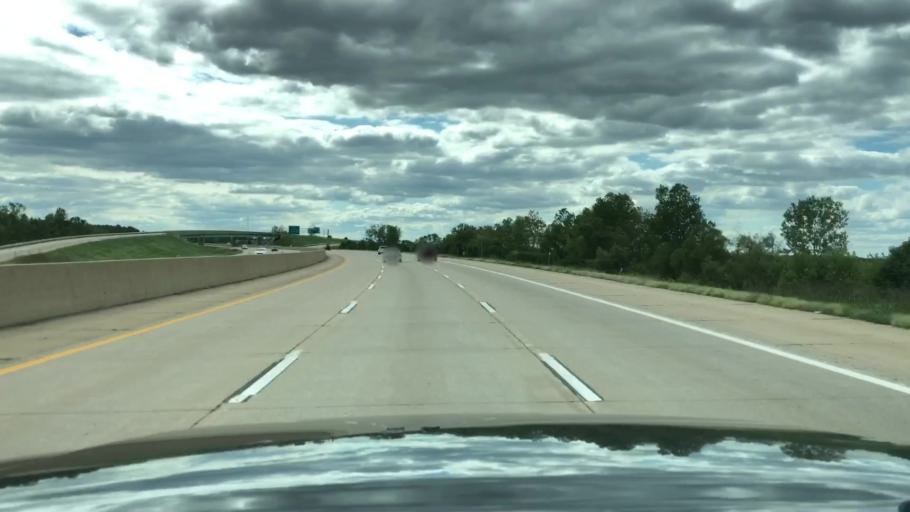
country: US
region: Missouri
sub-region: Saint Charles County
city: Saint Peters
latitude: 38.8144
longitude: -90.5816
